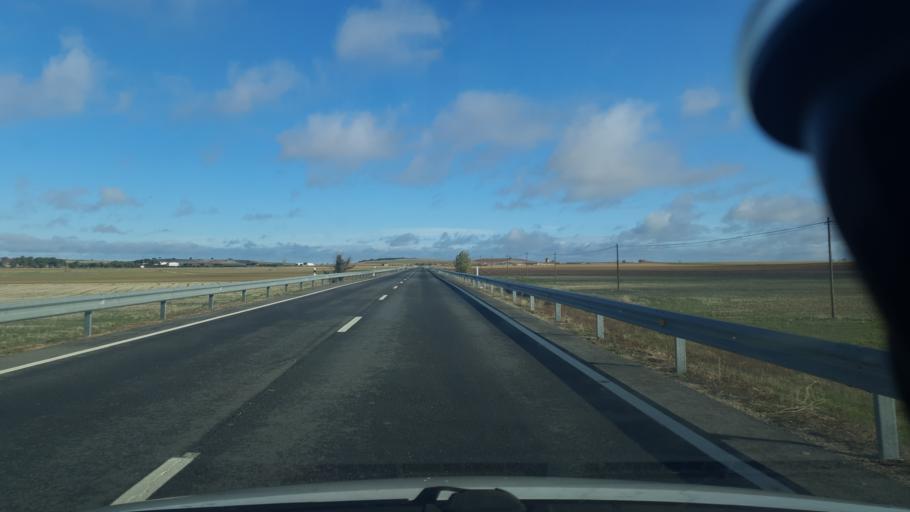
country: ES
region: Castille and Leon
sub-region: Provincia de Segovia
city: Codorniz
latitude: 41.0563
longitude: -4.6181
